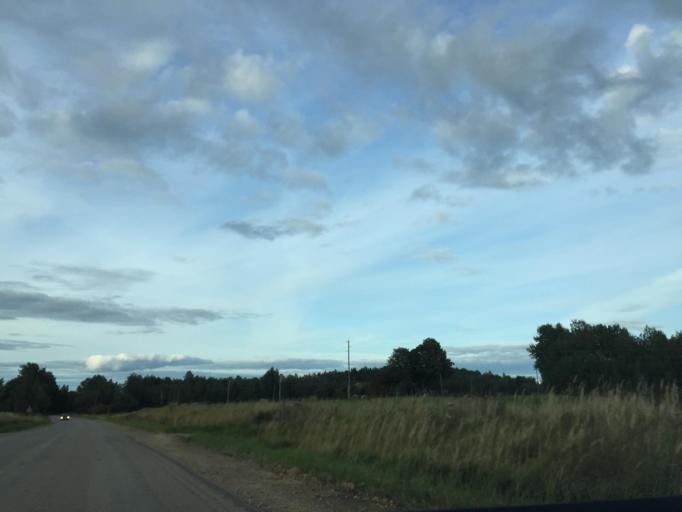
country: LV
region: Nereta
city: Nereta
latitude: 56.2901
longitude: 25.4131
